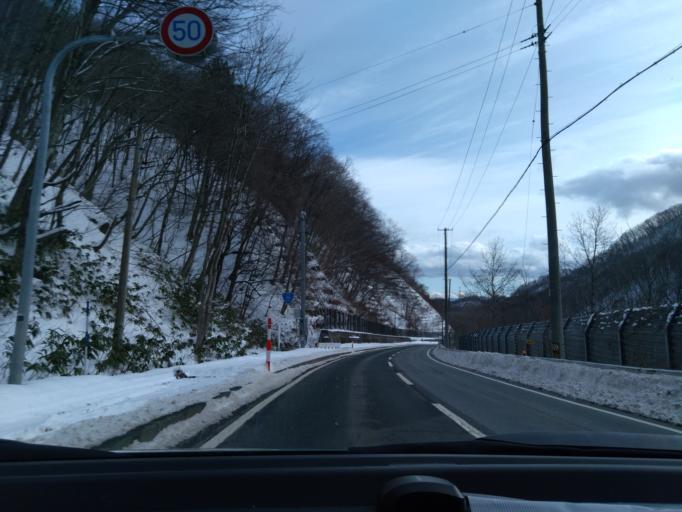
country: JP
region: Iwate
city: Shizukuishi
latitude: 39.7197
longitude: 140.8439
